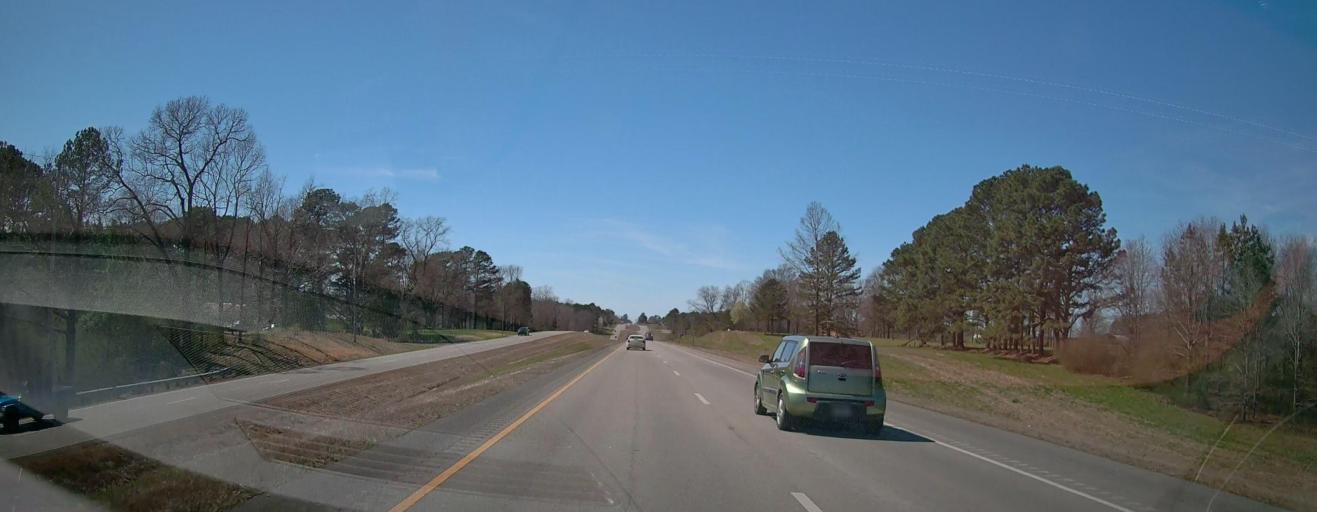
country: US
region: Alabama
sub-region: Cullman County
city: Cullman
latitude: 34.1761
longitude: -86.7210
